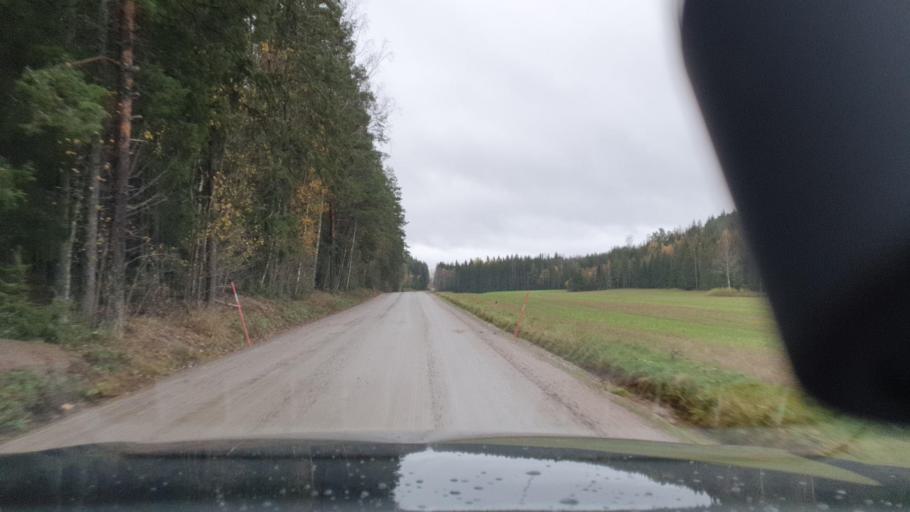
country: SE
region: Vaermland
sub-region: Arvika Kommun
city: Arvika
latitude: 59.6175
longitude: 12.8984
